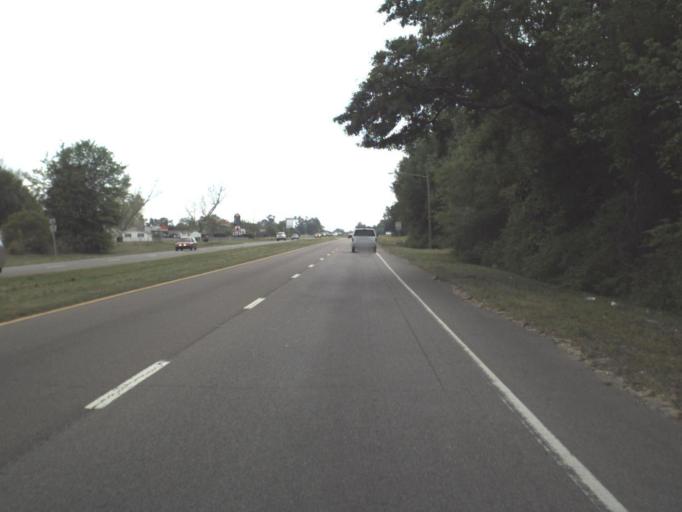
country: US
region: Florida
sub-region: Escambia County
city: Cantonment
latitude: 30.6038
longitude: -87.3157
